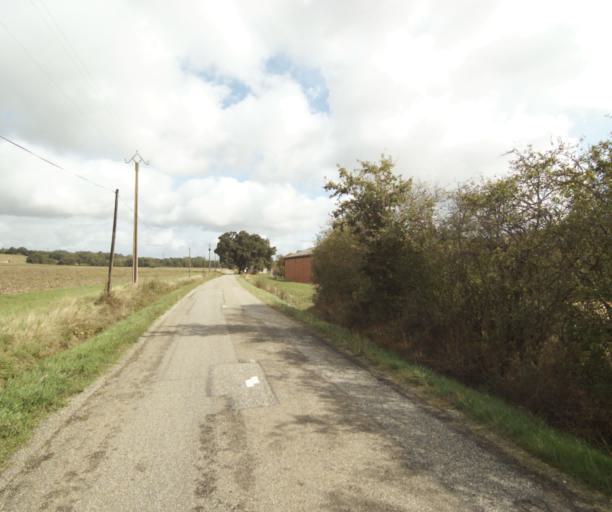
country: FR
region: Midi-Pyrenees
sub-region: Departement du Tarn-et-Garonne
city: Finhan
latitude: 43.8709
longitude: 1.1209
